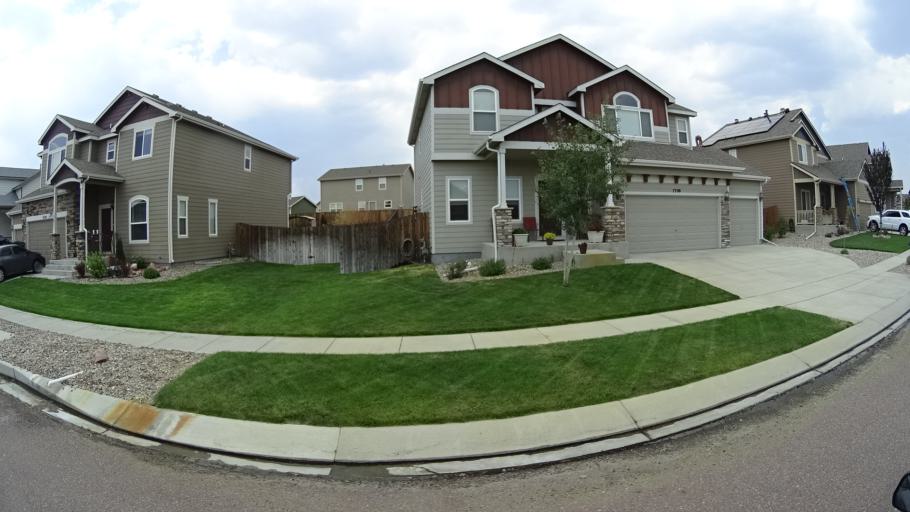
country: US
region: Colorado
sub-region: El Paso County
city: Black Forest
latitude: 38.9443
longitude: -104.6992
